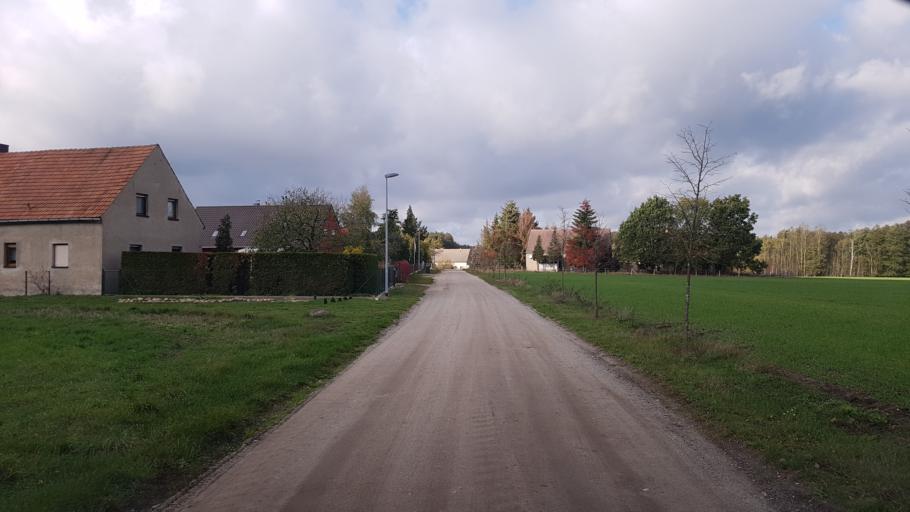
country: DE
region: Brandenburg
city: Schonborn
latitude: 51.6114
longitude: 13.5181
